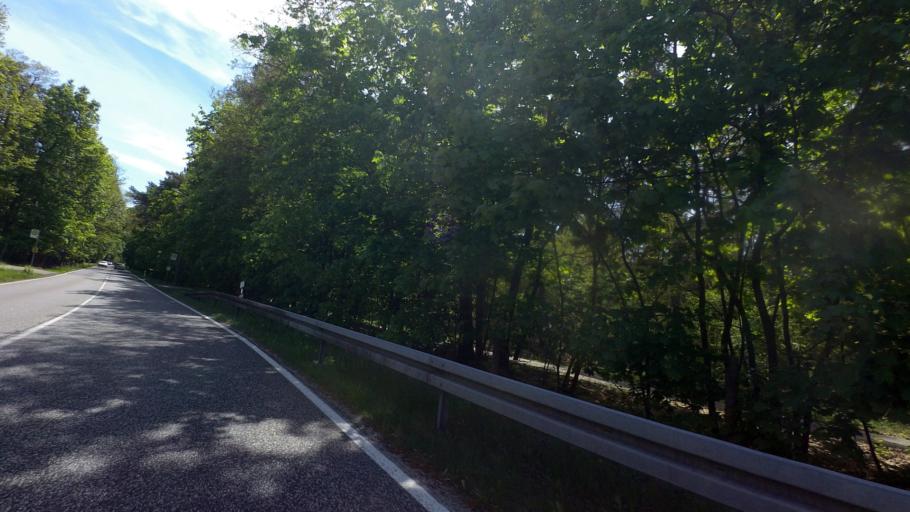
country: DE
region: Brandenburg
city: Luckenwalde
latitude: 52.1135
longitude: 13.1407
